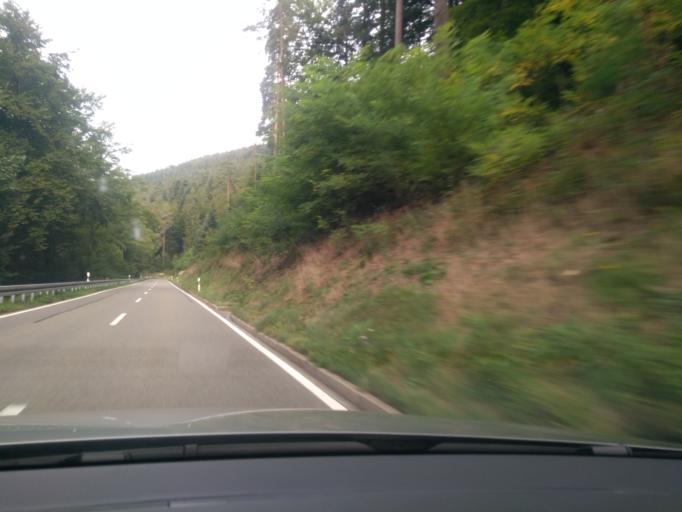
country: DE
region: Baden-Wuerttemberg
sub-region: Karlsruhe Region
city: Hofen an der Enz
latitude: 48.7994
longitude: 8.6055
